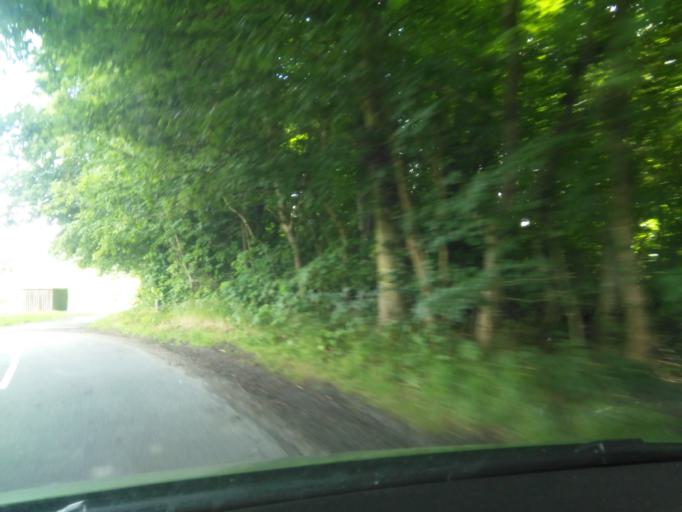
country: DK
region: Central Jutland
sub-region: Arhus Kommune
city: Logten
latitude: 56.2509
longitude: 10.3202
